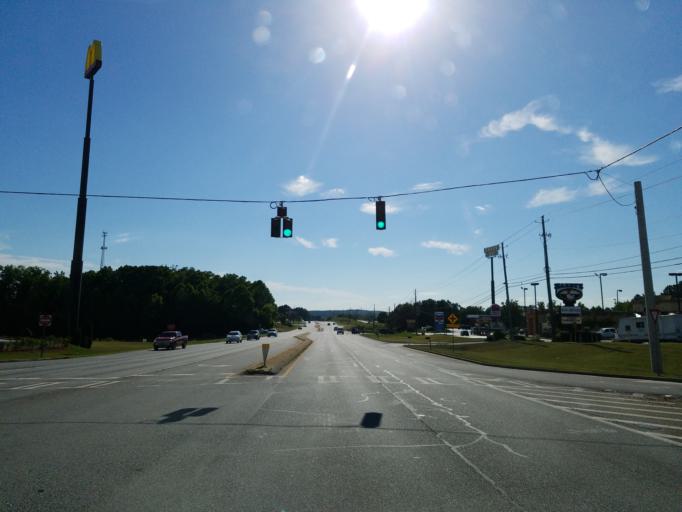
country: US
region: Georgia
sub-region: Bartow County
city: Adairsville
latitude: 34.3770
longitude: -84.9143
